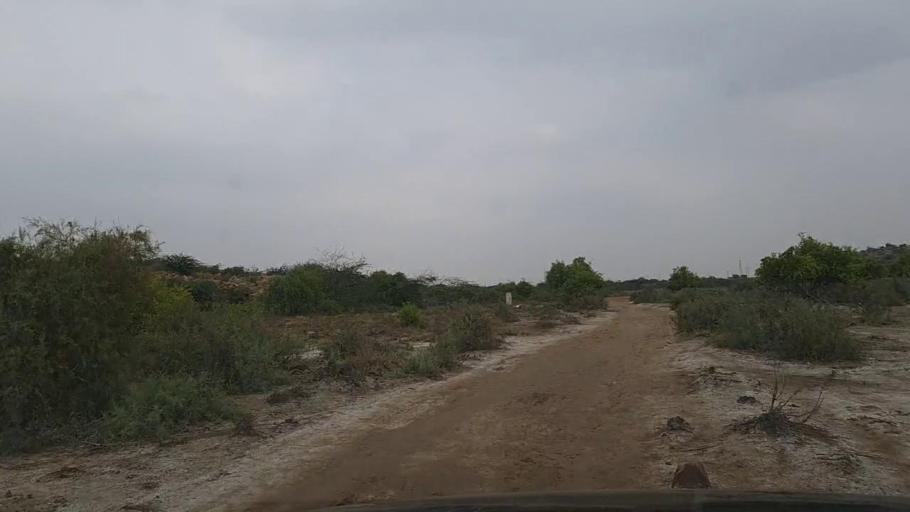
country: PK
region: Sindh
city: Thatta
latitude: 24.8185
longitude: 67.8248
